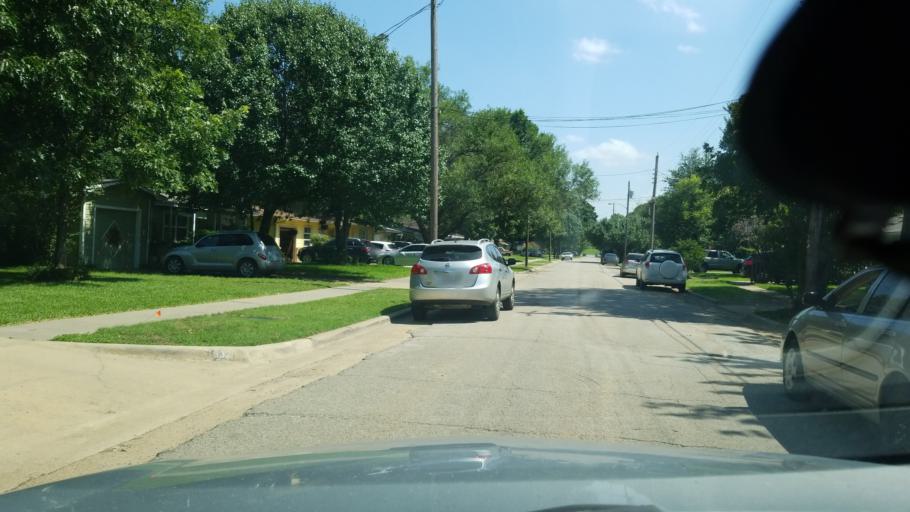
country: US
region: Texas
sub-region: Dallas County
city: Irving
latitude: 32.8202
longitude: -96.9608
